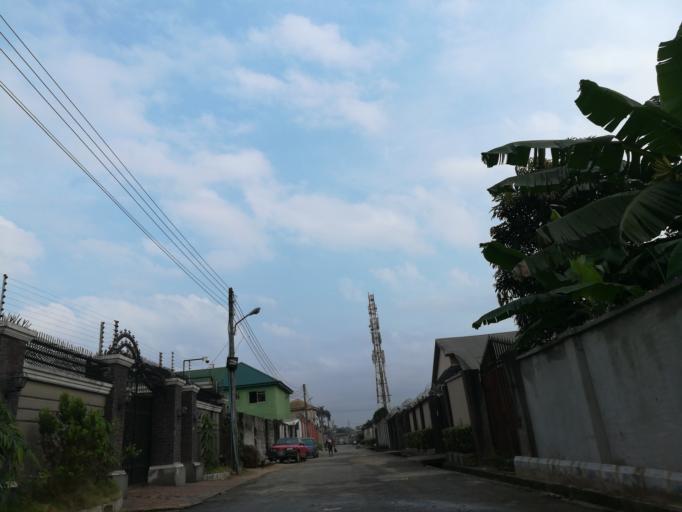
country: NG
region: Rivers
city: Port Harcourt
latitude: 4.8426
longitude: 7.0545
